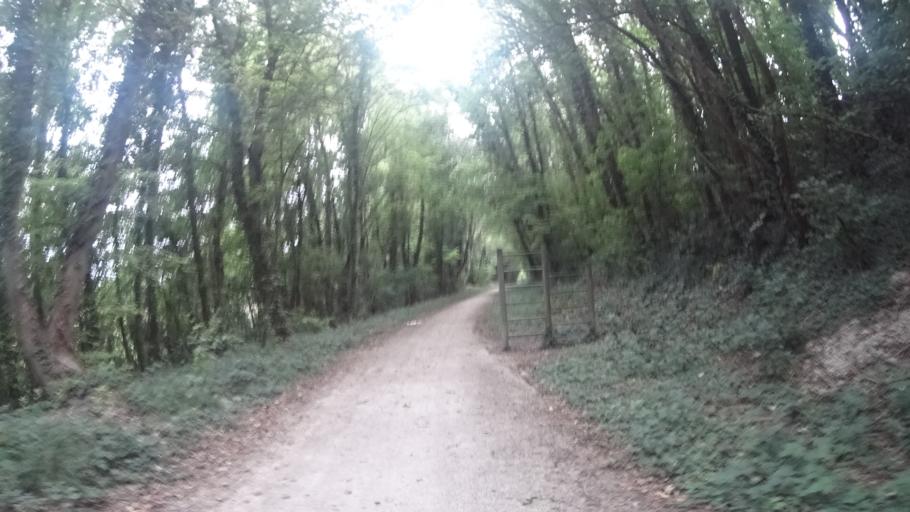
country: FR
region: Picardie
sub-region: Departement de l'Aisne
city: Origny-Sainte-Benoite
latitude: 49.8527
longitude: 3.4984
